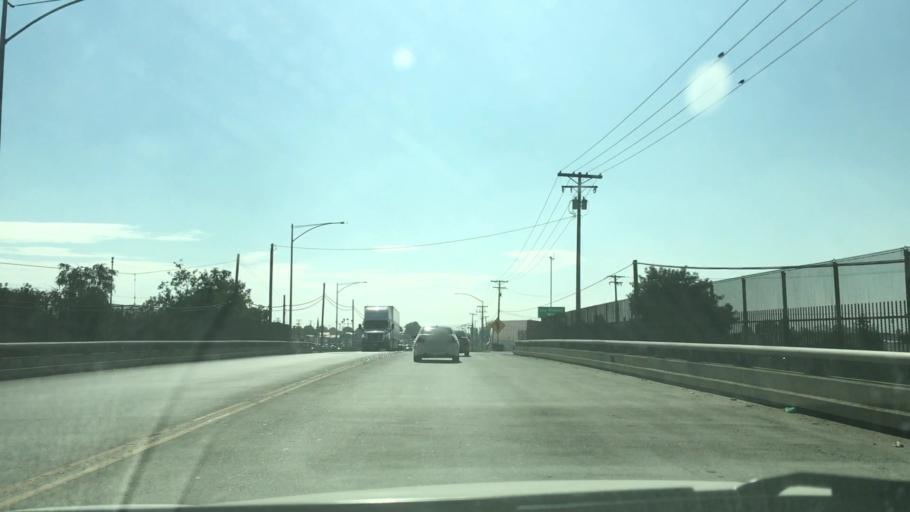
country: US
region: California
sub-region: Stanislaus County
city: Shackelford
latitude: 37.6188
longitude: -120.9936
